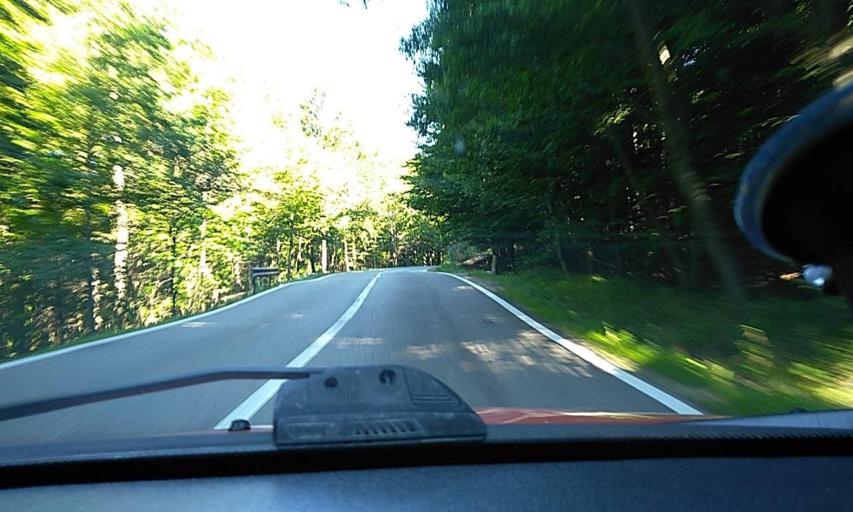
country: RO
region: Brasov
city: Crivina
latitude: 45.4645
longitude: 25.9414
